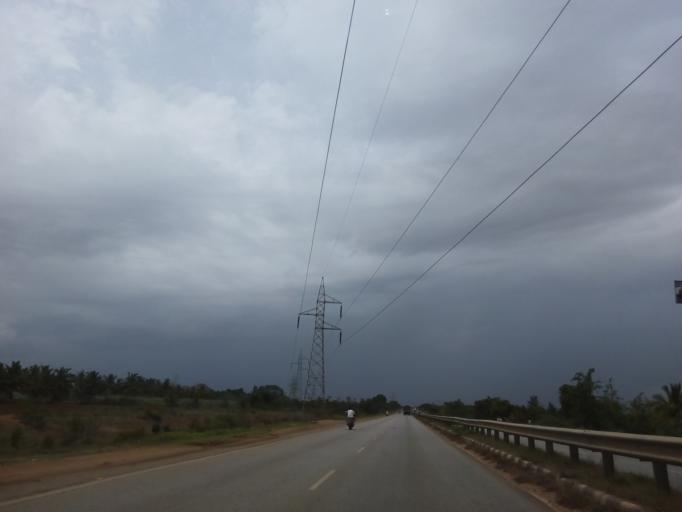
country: IN
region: Karnataka
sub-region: Davanagere
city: Harihar
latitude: 14.4813
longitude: 75.8089
